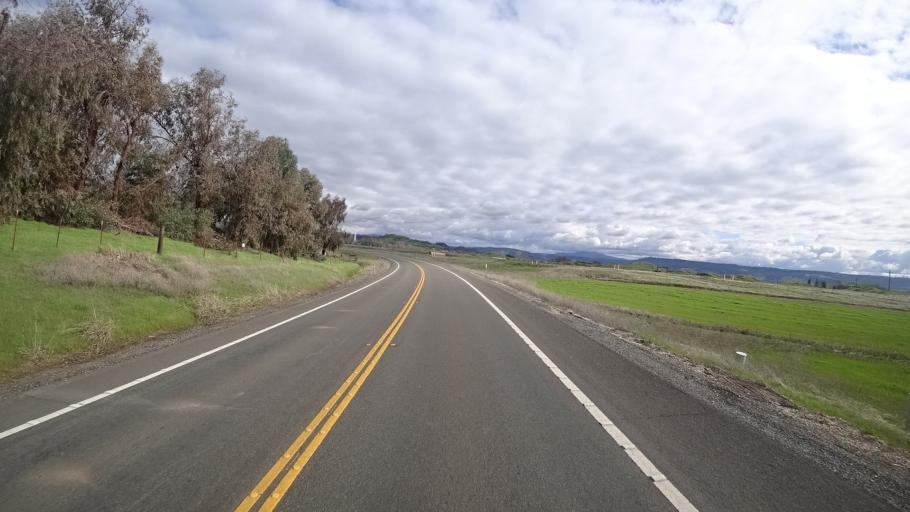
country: US
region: California
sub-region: Butte County
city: Paradise
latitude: 39.6423
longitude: -121.6422
